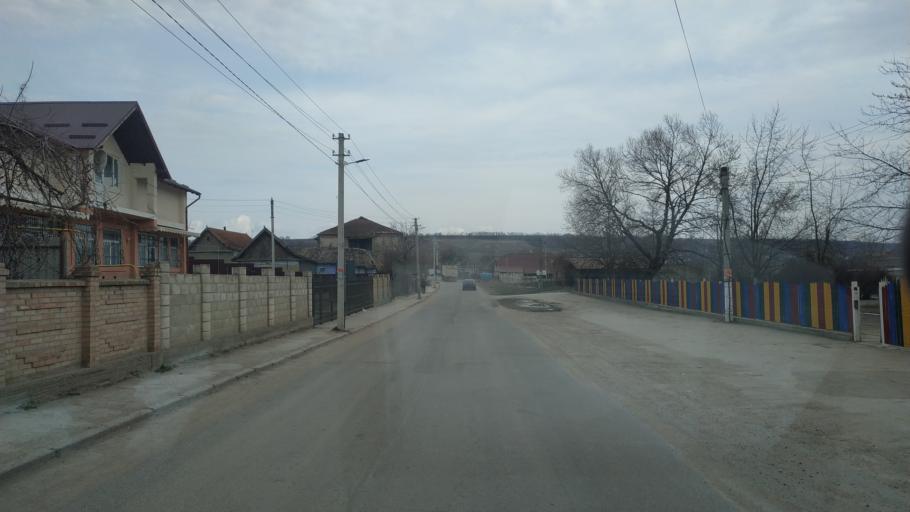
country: MD
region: Anenii Noi
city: Varnita
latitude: 46.8408
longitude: 29.3602
